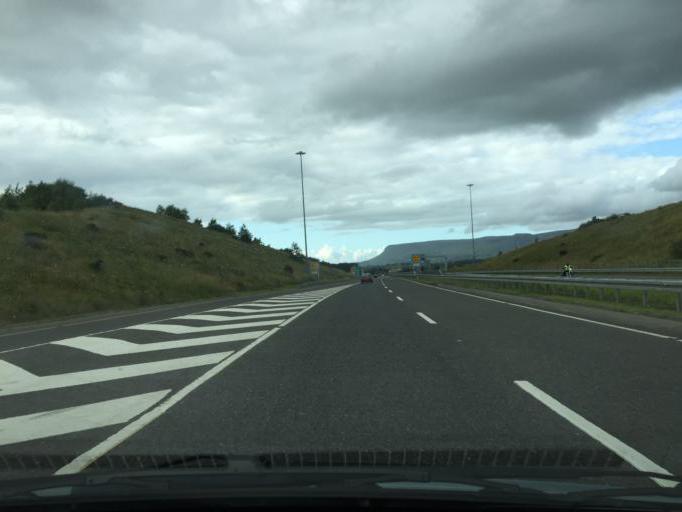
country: IE
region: Connaught
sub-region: Sligo
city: Sligo
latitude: 54.2618
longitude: -8.4812
